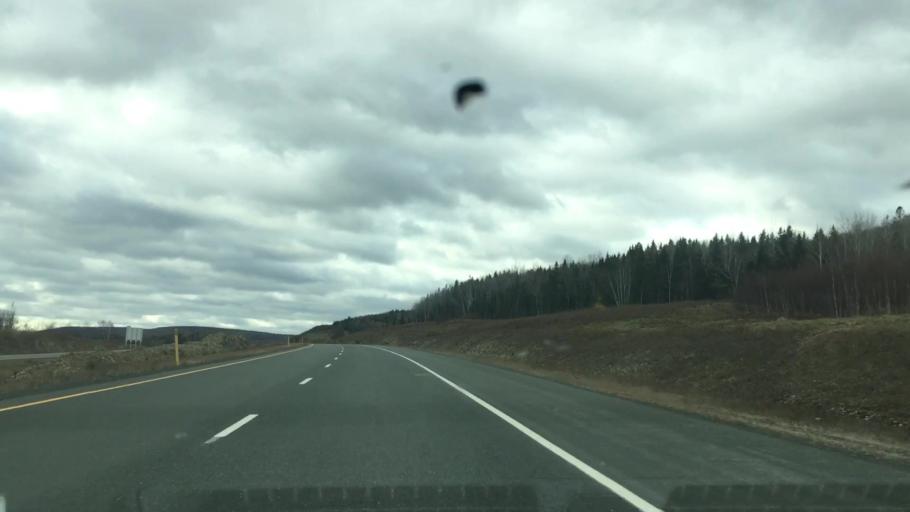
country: US
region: Maine
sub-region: Aroostook County
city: Fort Fairfield
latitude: 46.7260
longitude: -67.7282
